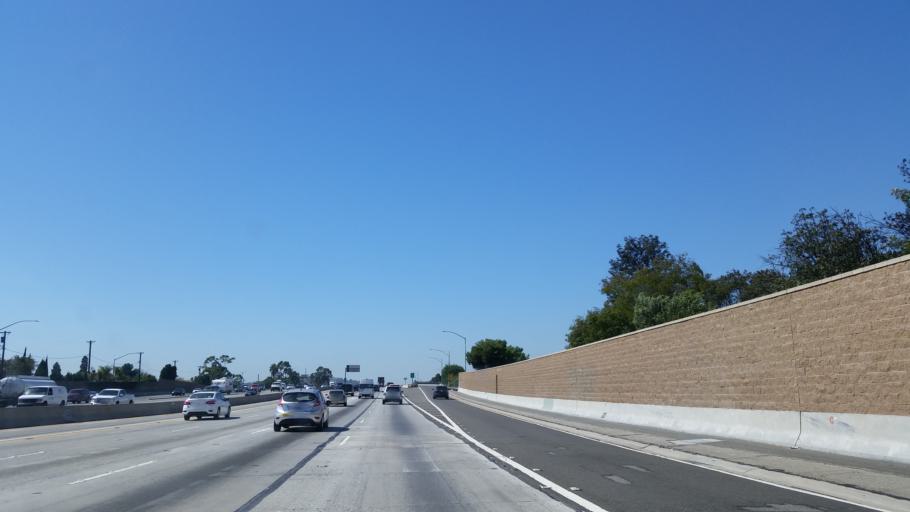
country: US
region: California
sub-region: Orange County
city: Rossmoor
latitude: 33.8029
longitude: -118.1206
